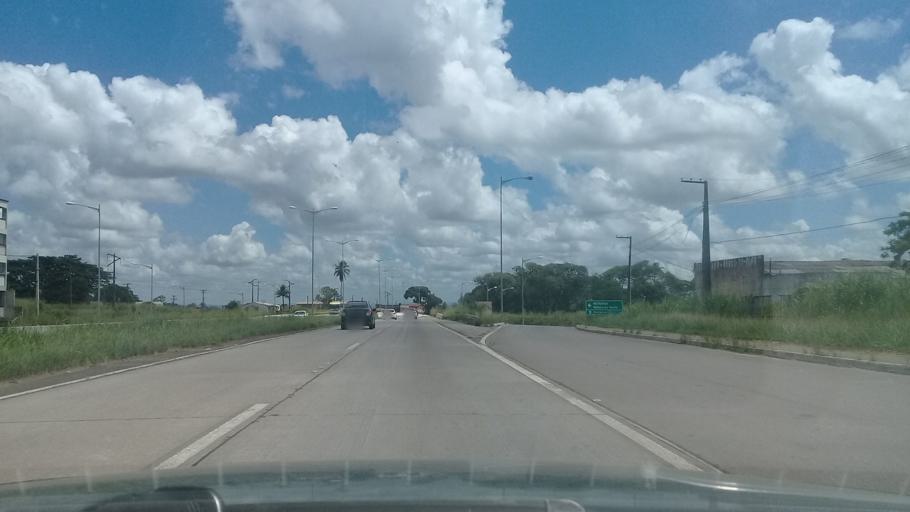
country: BR
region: Pernambuco
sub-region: Carpina
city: Carpina
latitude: -7.9179
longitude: -35.1651
